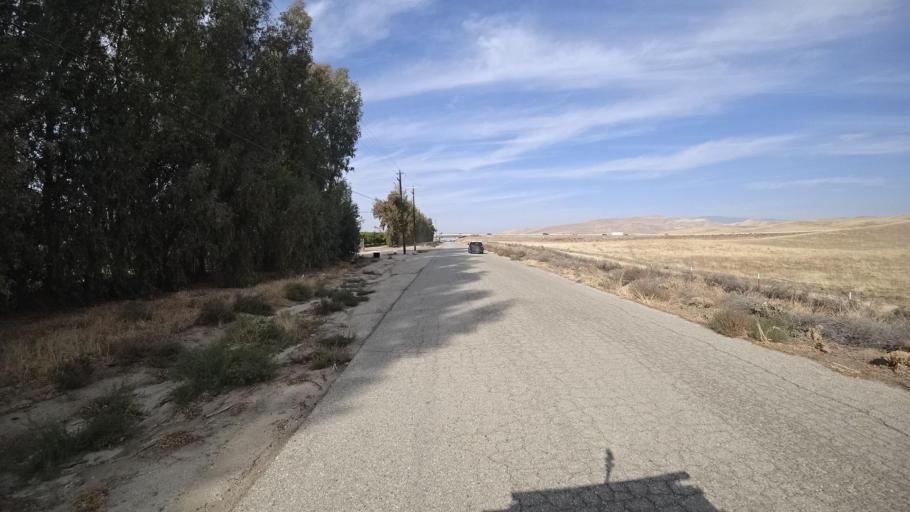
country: US
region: California
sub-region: Kern County
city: Arvin
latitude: 35.2892
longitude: -118.7527
